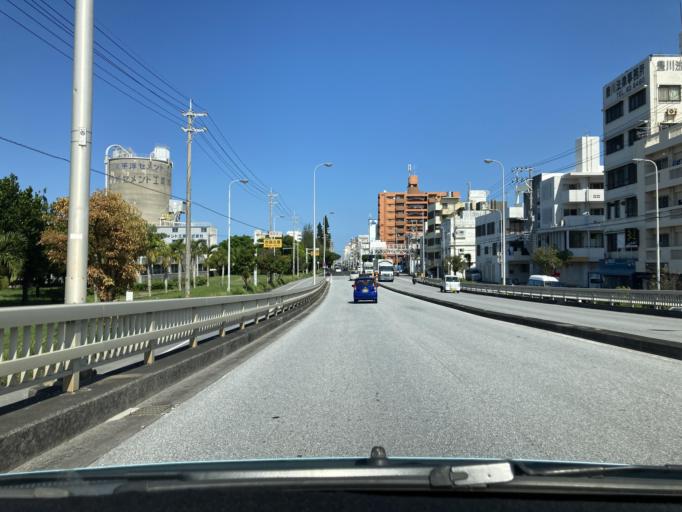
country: JP
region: Okinawa
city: Naha-shi
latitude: 26.2313
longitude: 127.6816
